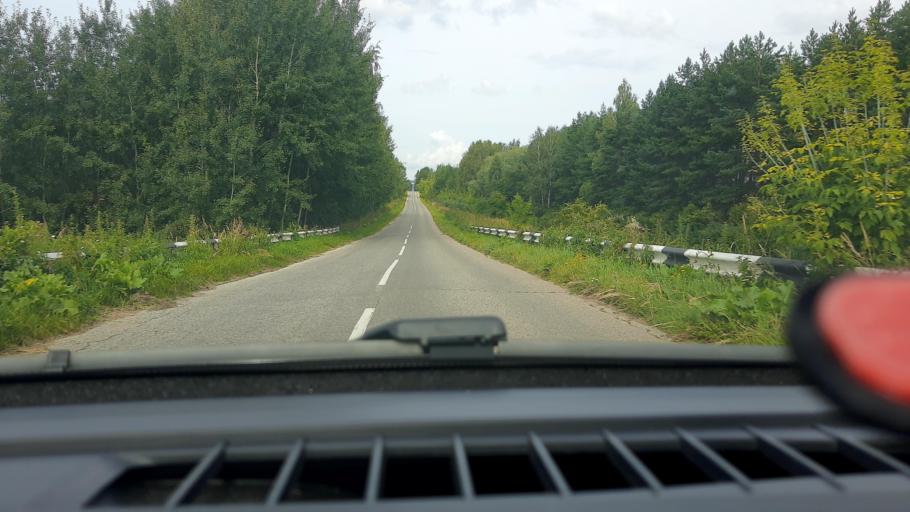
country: RU
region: Nizjnij Novgorod
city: Burevestnik
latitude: 56.0459
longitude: 43.7104
